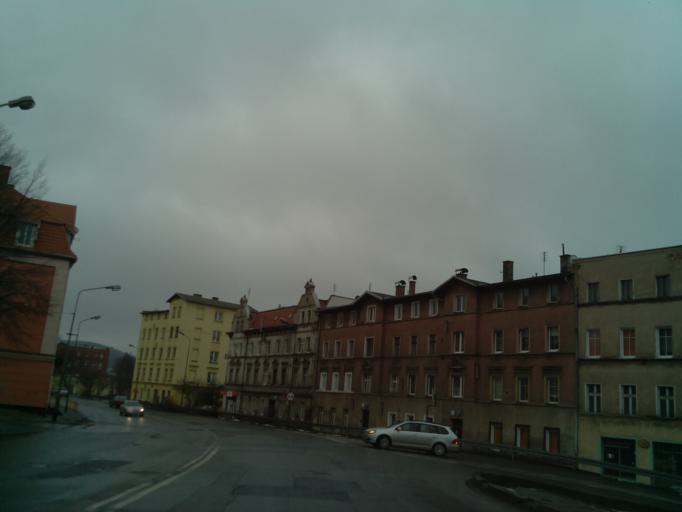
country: PL
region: Lower Silesian Voivodeship
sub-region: Powiat walbrzyski
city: Szczawno-Zdroj
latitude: 50.8197
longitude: 16.3005
